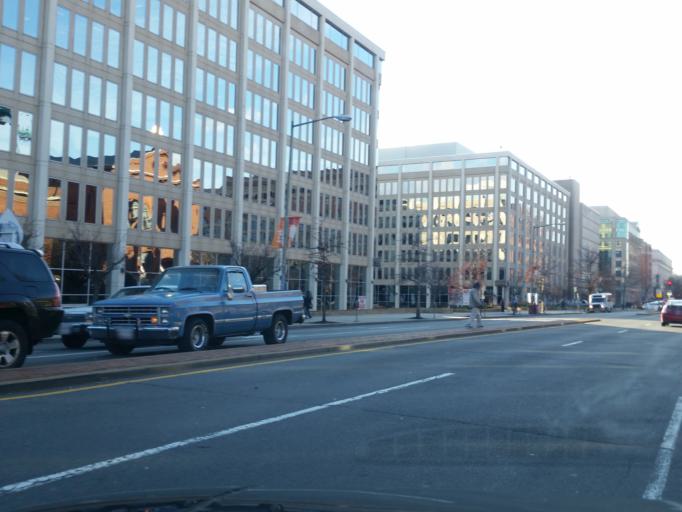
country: US
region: Washington, D.C.
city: Washington, D.C.
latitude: 38.9024
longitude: -77.0092
